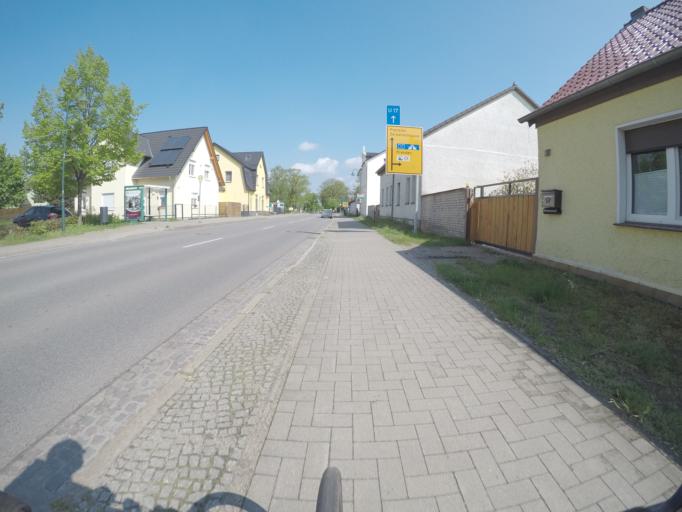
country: DE
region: Brandenburg
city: Wandlitz
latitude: 52.7898
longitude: 13.4804
